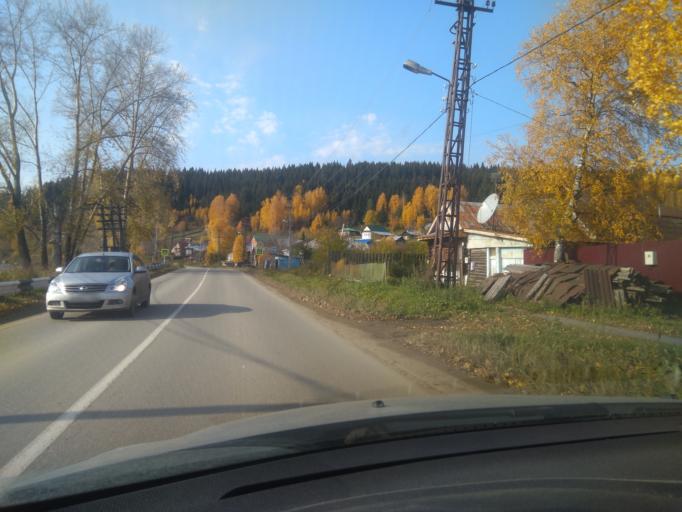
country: RU
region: Sverdlovsk
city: Nizhniye Sergi
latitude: 56.6756
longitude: 59.3231
